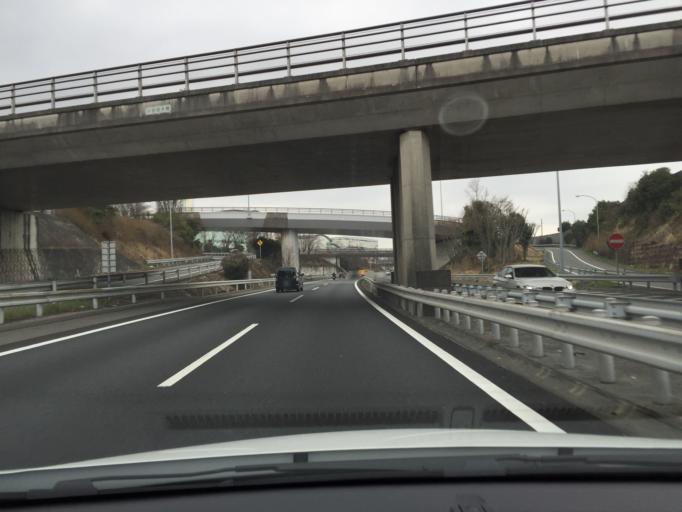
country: JP
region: Saitama
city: Sayama
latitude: 35.8193
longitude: 139.3700
